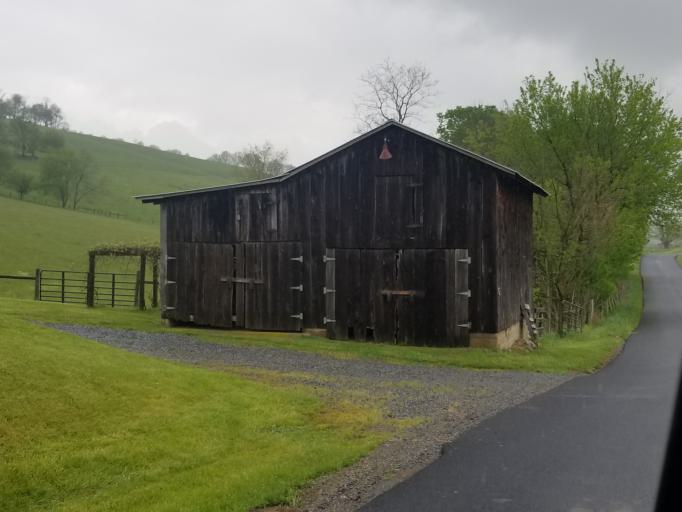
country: US
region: Virginia
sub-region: Smyth County
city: Marion
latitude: 36.9177
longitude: -81.5667
